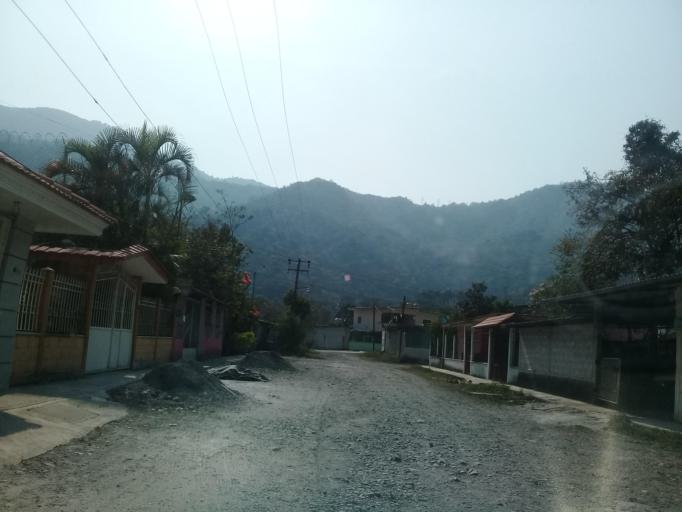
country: MX
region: Veracruz
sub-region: Ixtaczoquitlan
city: Campo Chico
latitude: 18.8363
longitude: -97.0298
